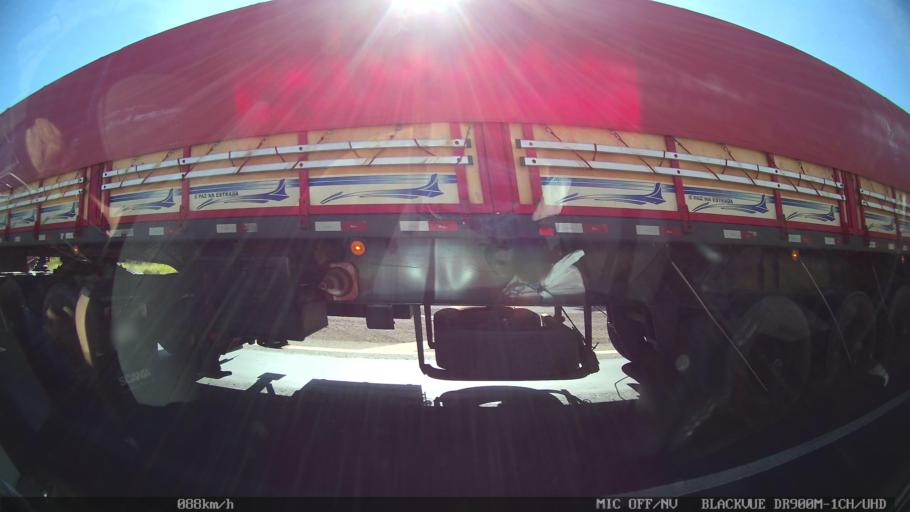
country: BR
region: Sao Paulo
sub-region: Barretos
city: Barretos
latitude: -20.6086
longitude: -48.7473
